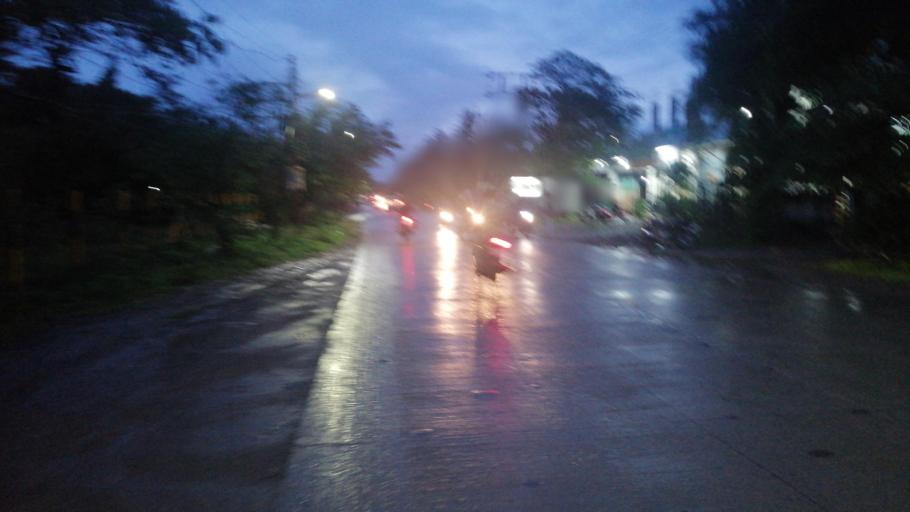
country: IN
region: Maharashtra
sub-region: Aurangabad Division
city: Aurangabad
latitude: 19.8791
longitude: 75.3766
